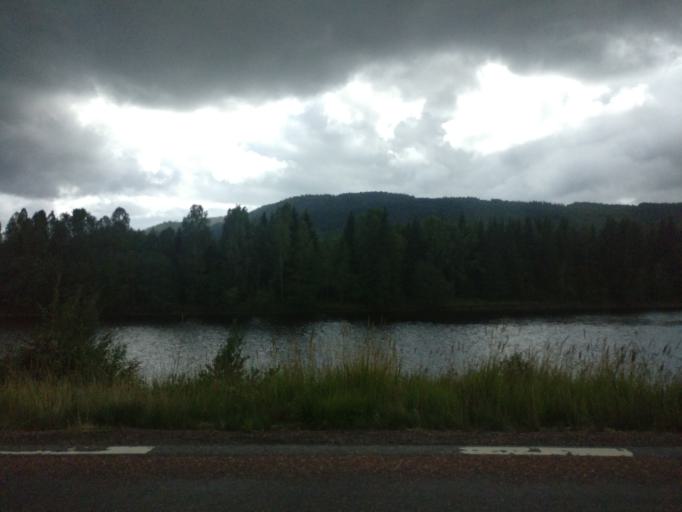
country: SE
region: Vaermland
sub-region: Torsby Kommun
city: Torsby
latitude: 60.7394
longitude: 12.8501
